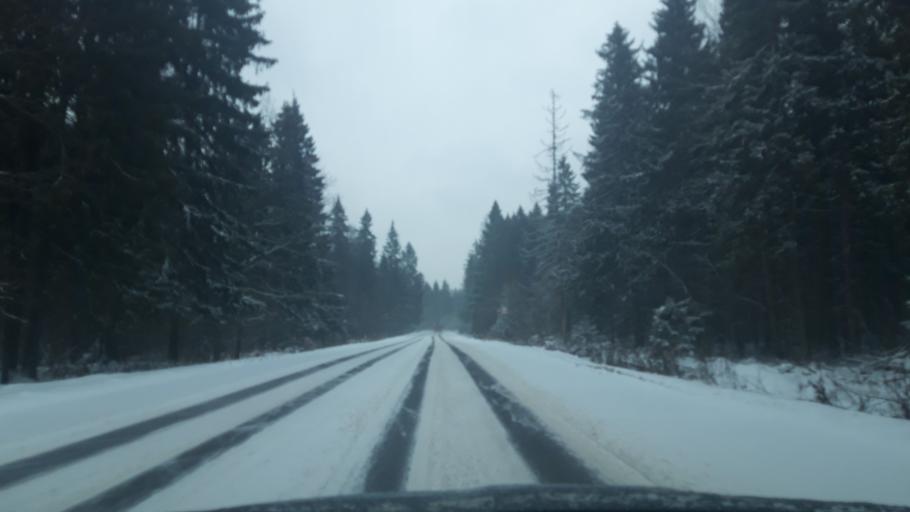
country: RU
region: Moskovskaya
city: Avtopoligon
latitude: 56.2845
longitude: 37.3788
